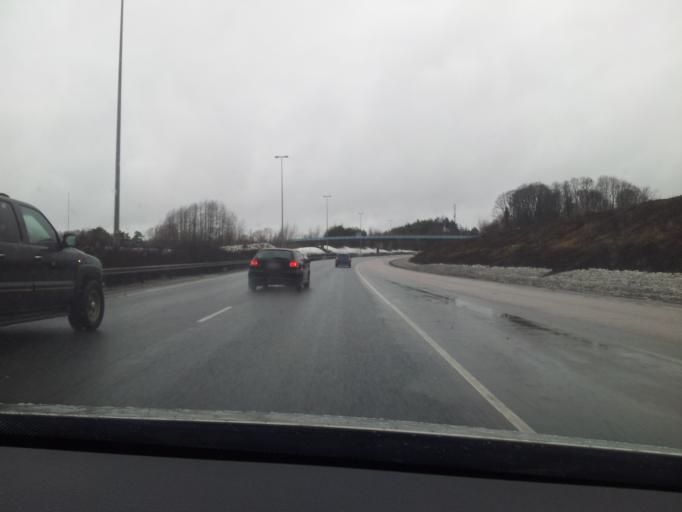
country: FI
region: Uusimaa
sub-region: Helsinki
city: Kauniainen
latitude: 60.1915
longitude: 24.7458
